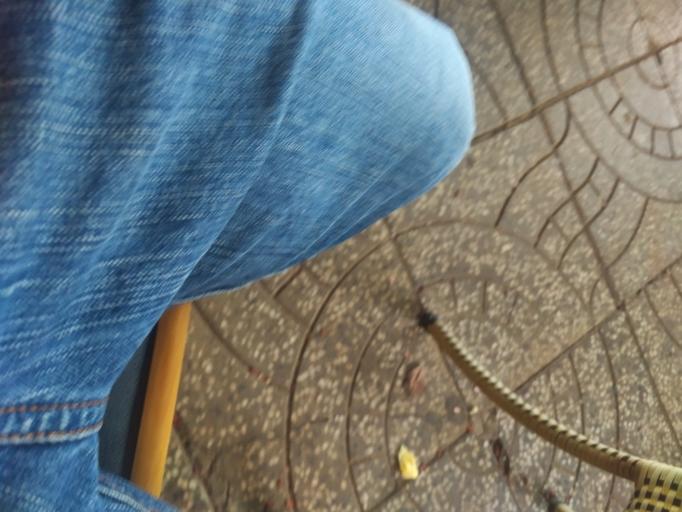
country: VN
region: Dak Nong
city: Gia Nghia
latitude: 12.0100
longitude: 107.6858
